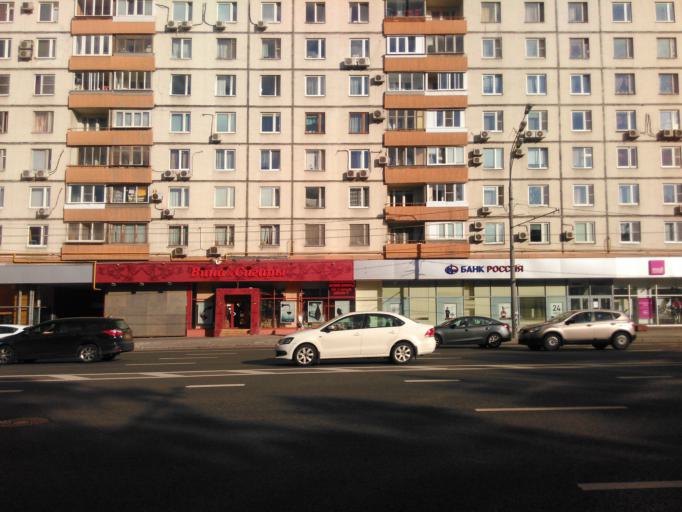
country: RU
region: Moscow
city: Zamoskvorech'ye
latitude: 55.7261
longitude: 37.6073
